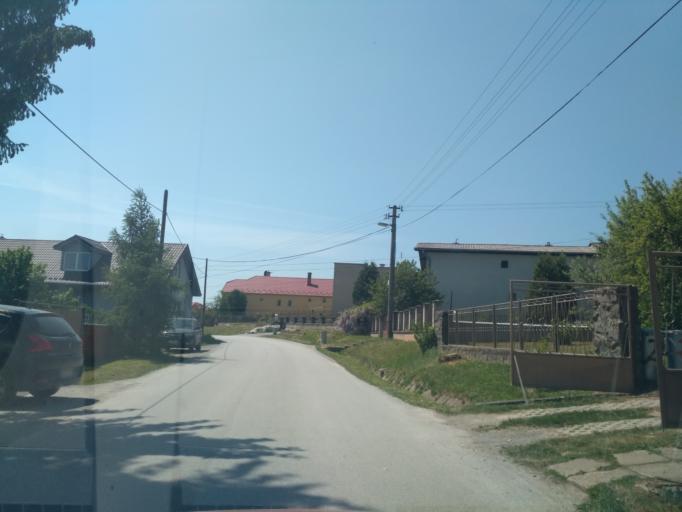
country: SK
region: Kosicky
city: Kosice
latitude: 48.7916
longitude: 21.3474
